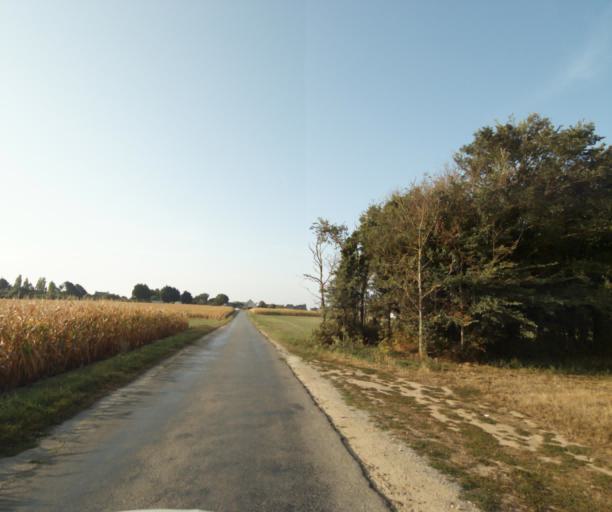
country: FR
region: Brittany
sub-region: Departement du Morbihan
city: Riantec
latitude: 47.7071
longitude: -3.2963
